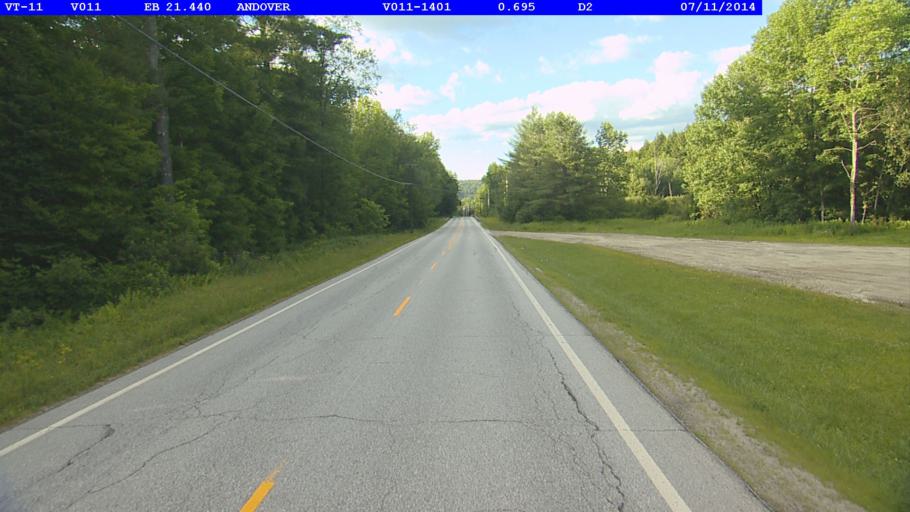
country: US
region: Vermont
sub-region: Windsor County
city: Chester
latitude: 43.2423
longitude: -72.7239
